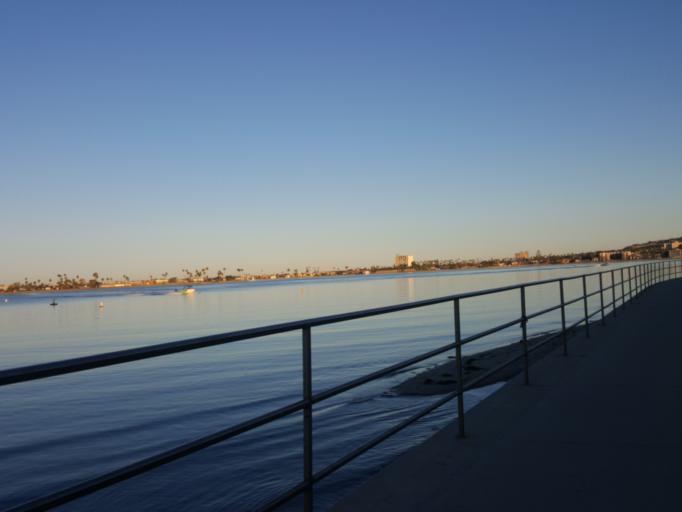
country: US
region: California
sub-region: San Diego County
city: La Jolla
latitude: 32.7810
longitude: -117.2389
